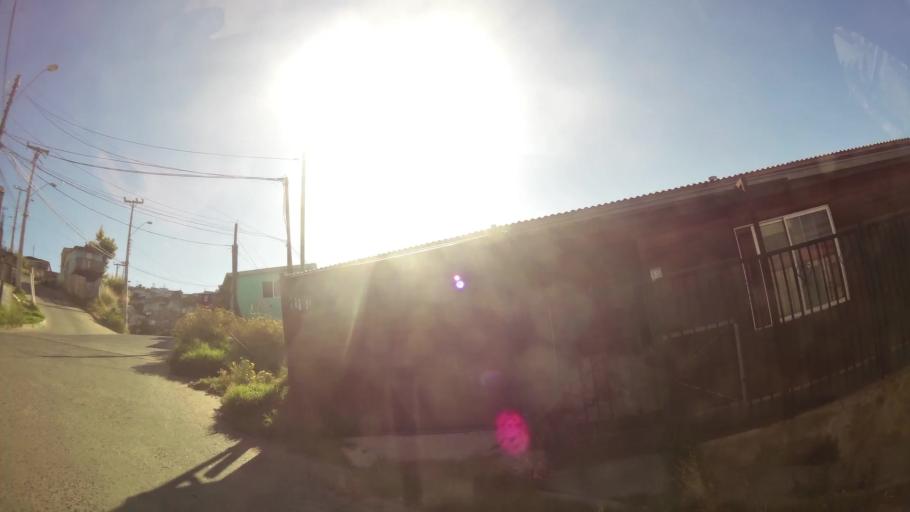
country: CL
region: Valparaiso
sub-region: Provincia de Valparaiso
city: Valparaiso
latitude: -33.0598
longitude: -71.6197
